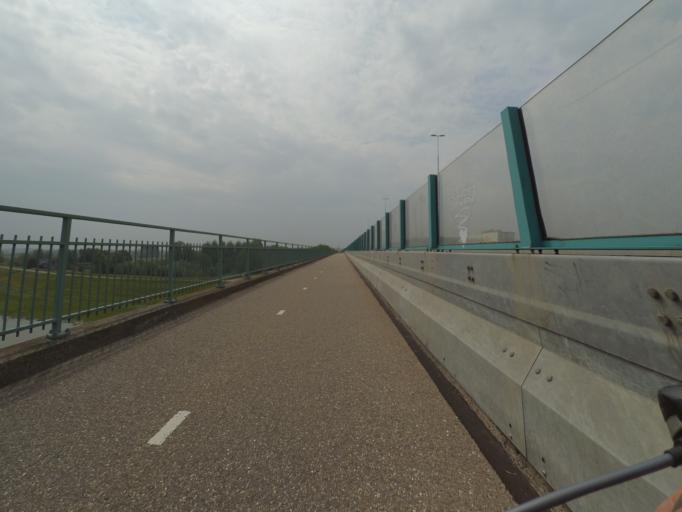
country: NL
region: Gelderland
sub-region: Gemeente Overbetuwe
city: Heteren
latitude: 51.9616
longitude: 5.7669
